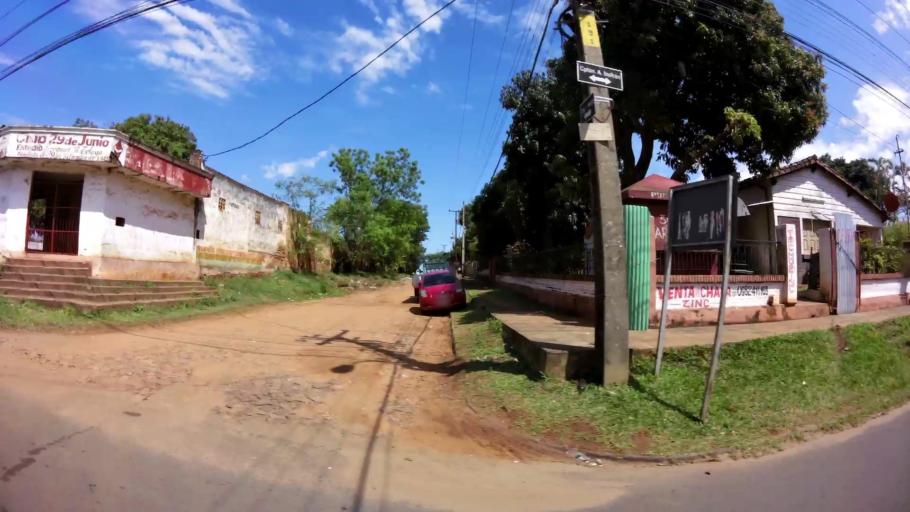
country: PY
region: Central
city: San Lorenzo
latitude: -25.2765
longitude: -57.4971
